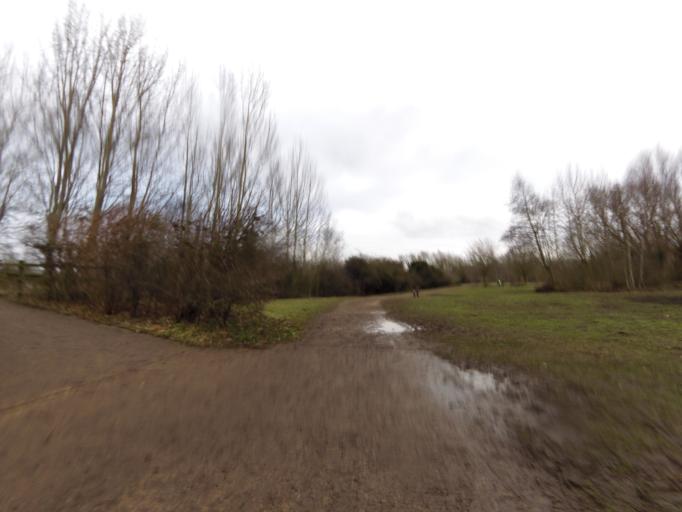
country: GB
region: England
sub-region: Cambridgeshire
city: Waterbeach
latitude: 52.2365
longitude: 0.1642
